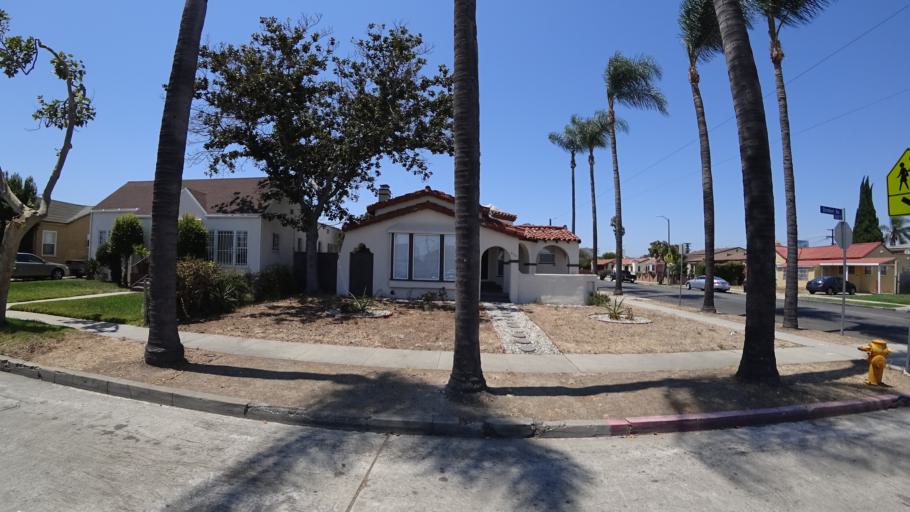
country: US
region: California
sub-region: Los Angeles County
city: Westmont
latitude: 33.9588
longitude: -118.3047
